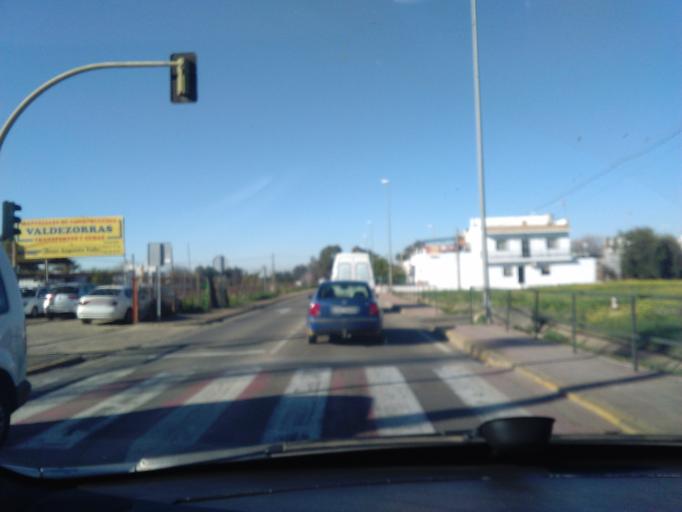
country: ES
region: Andalusia
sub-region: Provincia de Sevilla
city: Sevilla
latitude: 37.4271
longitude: -5.9296
